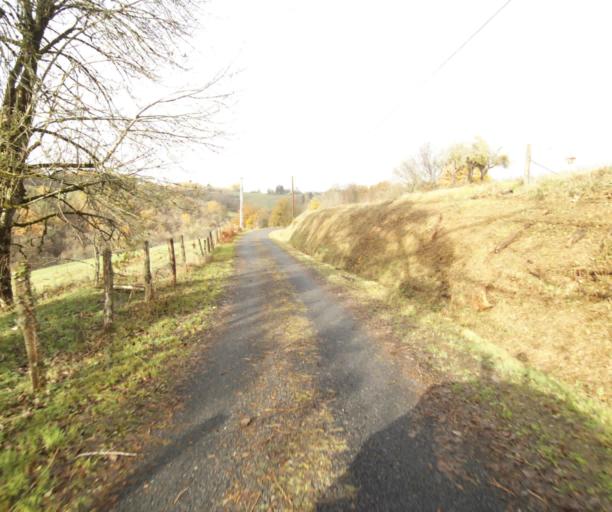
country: FR
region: Limousin
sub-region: Departement de la Correze
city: Cornil
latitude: 45.2244
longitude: 1.6431
